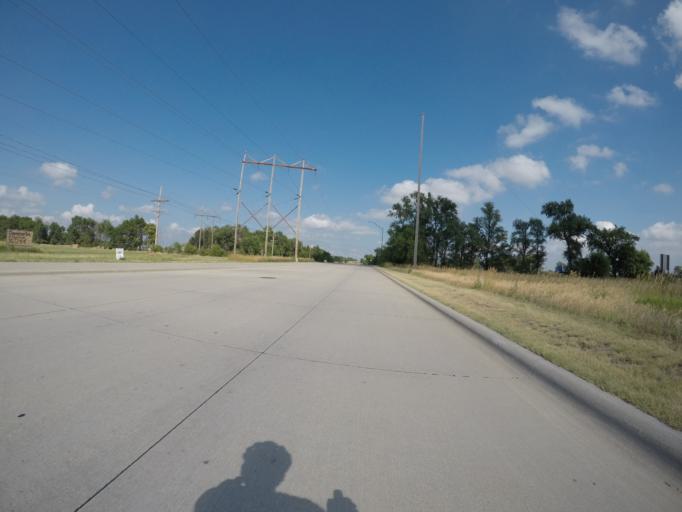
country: US
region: Nebraska
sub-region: Buffalo County
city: Kearney
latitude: 40.6706
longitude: -99.0735
